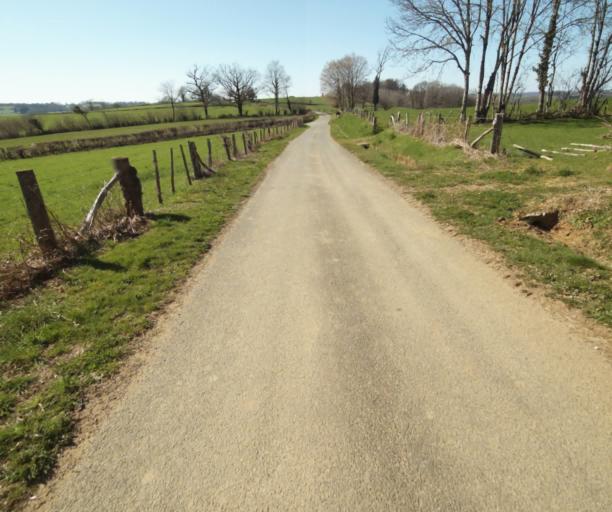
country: FR
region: Limousin
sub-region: Departement de la Correze
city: Uzerche
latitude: 45.4146
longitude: 1.6310
